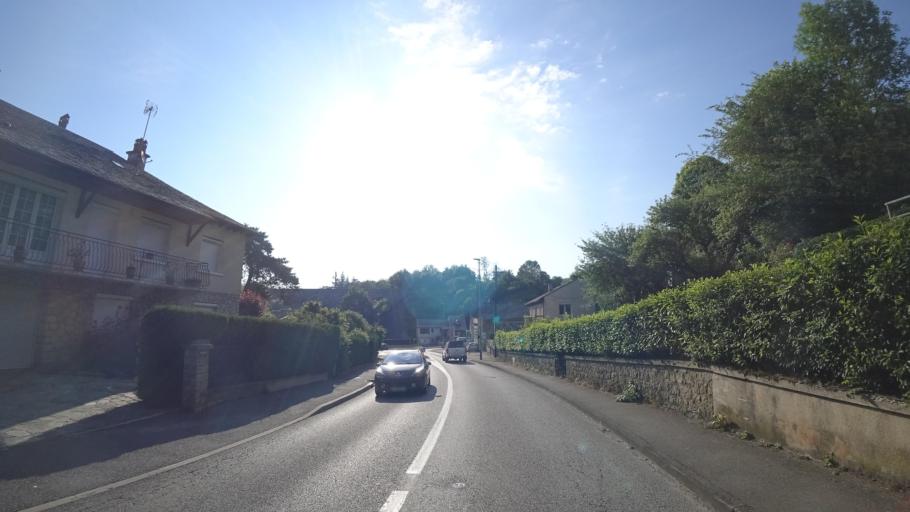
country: FR
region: Midi-Pyrenees
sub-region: Departement de l'Aveyron
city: Olemps
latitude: 44.3352
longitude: 2.5581
